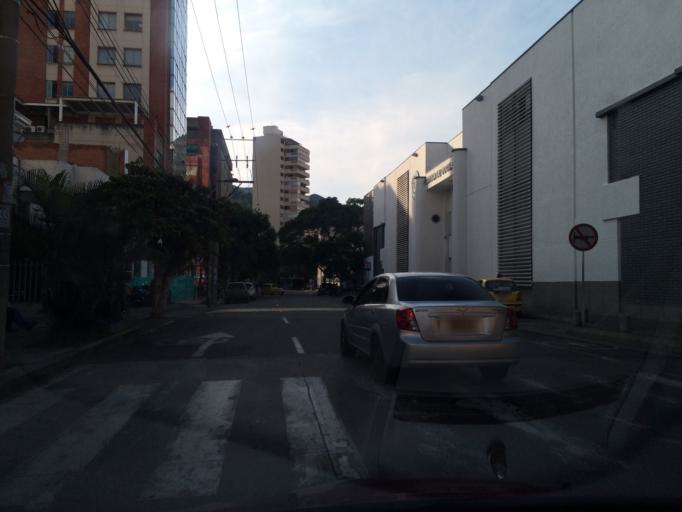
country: CO
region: Valle del Cauca
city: Cali
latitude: 3.4600
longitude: -76.5302
